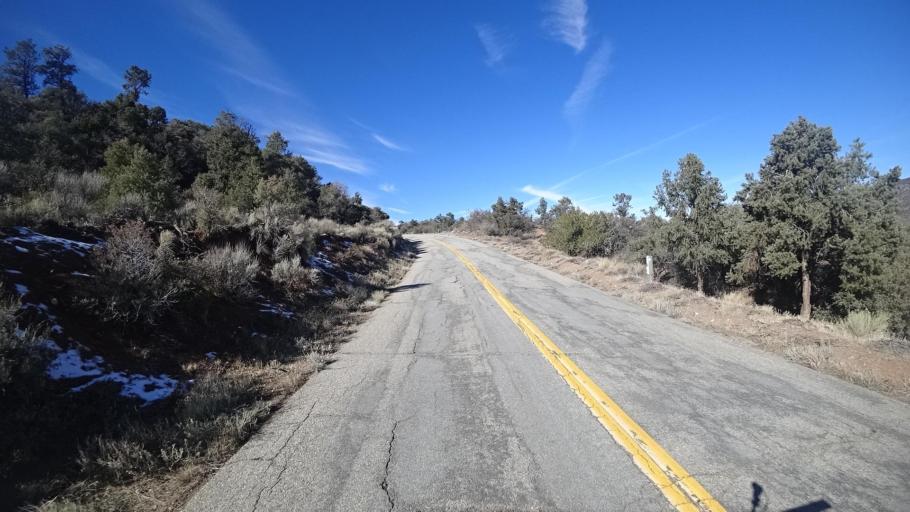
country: US
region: California
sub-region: Kern County
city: Pine Mountain Club
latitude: 34.8685
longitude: -119.2582
